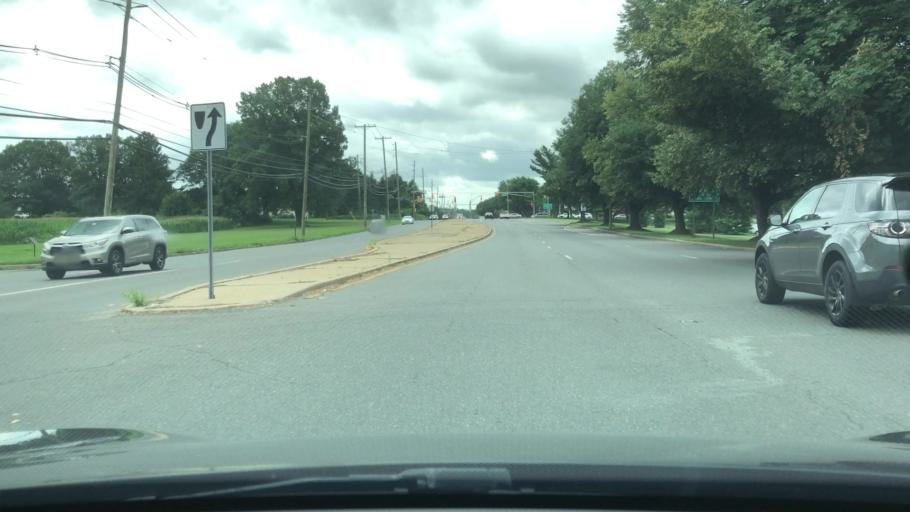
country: US
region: New Jersey
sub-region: Mercer County
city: Lawrenceville
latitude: 40.2919
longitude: -74.6776
